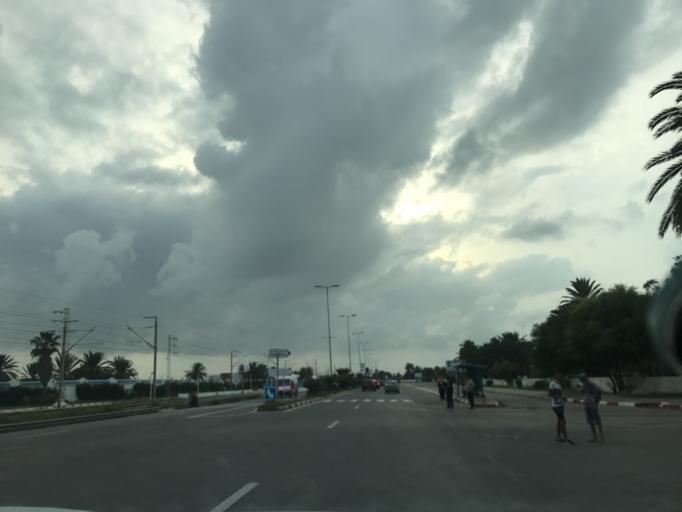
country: TN
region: Al Munastir
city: Sahline
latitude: 35.7609
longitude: 10.7470
